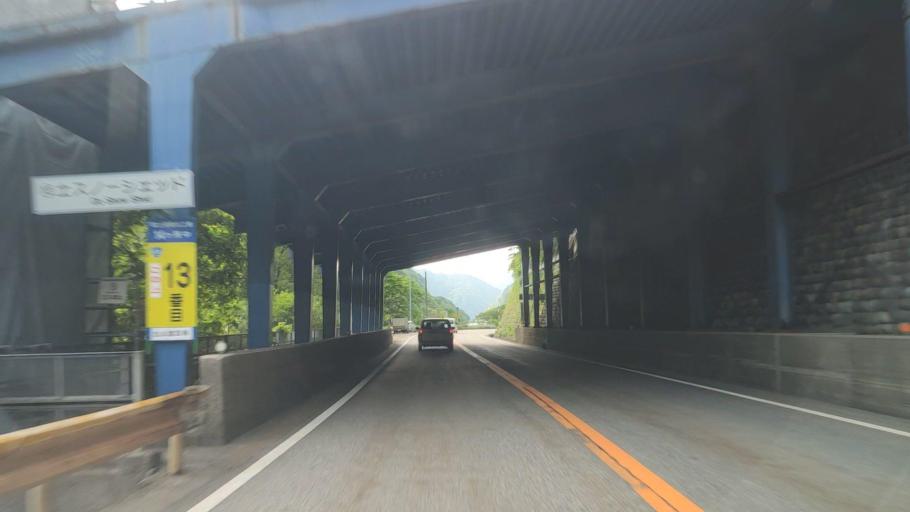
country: JP
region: Toyama
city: Yatsuomachi-higashikumisaka
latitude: 36.4129
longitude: 137.2917
